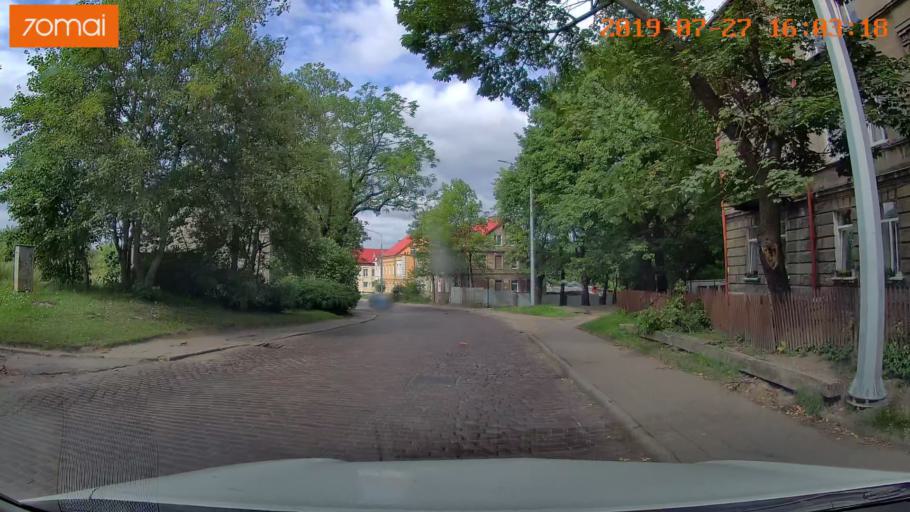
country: RU
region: Kaliningrad
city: Chernyakhovsk
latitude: 54.6318
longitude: 21.8029
